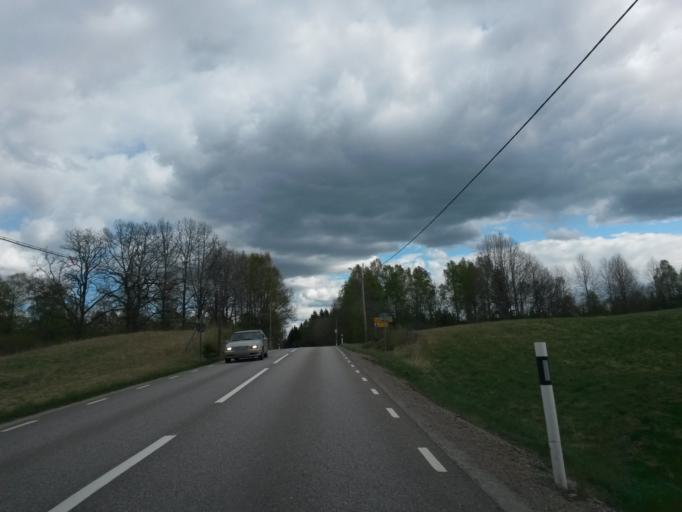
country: SE
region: Vaestra Goetaland
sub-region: Boras Kommun
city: Boras
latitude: 57.8450
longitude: 12.9610
